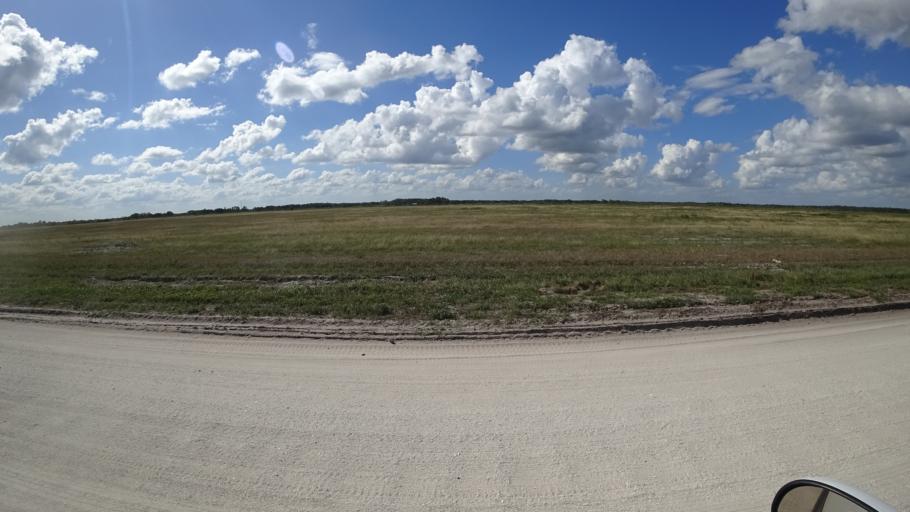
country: US
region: Florida
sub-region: DeSoto County
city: Arcadia
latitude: 27.3196
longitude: -82.1007
